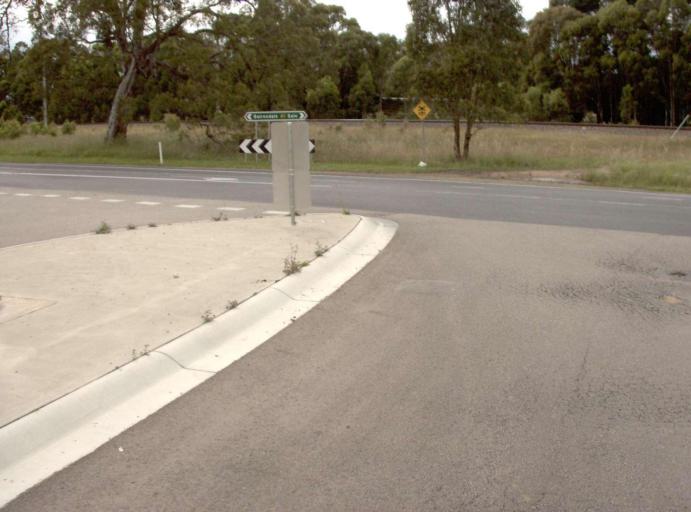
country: AU
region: Victoria
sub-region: East Gippsland
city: Bairnsdale
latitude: -37.8435
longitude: 147.5884
